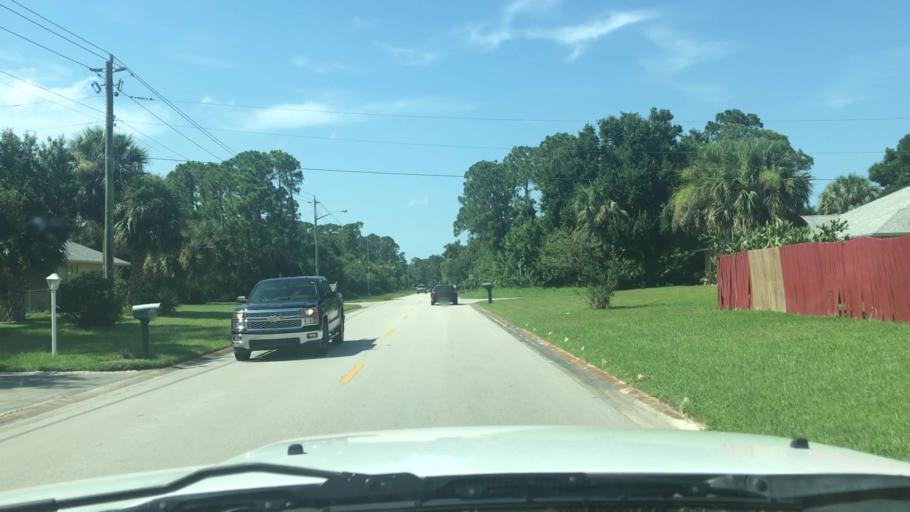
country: US
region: Florida
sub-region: Indian River County
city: Florida Ridge
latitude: 27.5679
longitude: -80.3980
